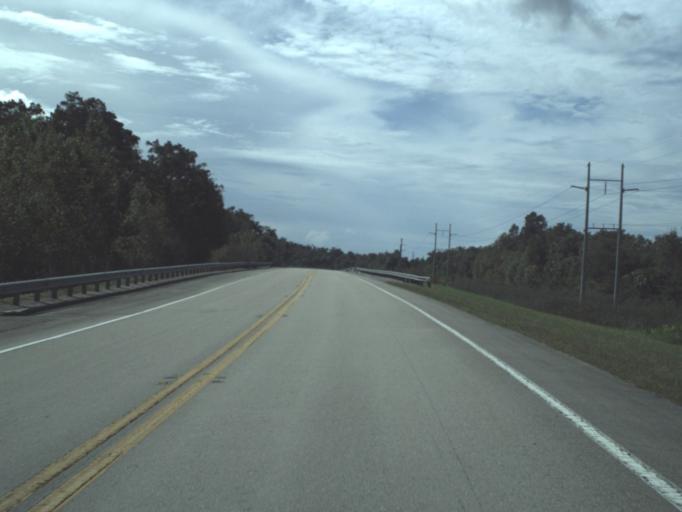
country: US
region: Florida
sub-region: Collier County
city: Orangetree
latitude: 26.0469
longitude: -81.3453
